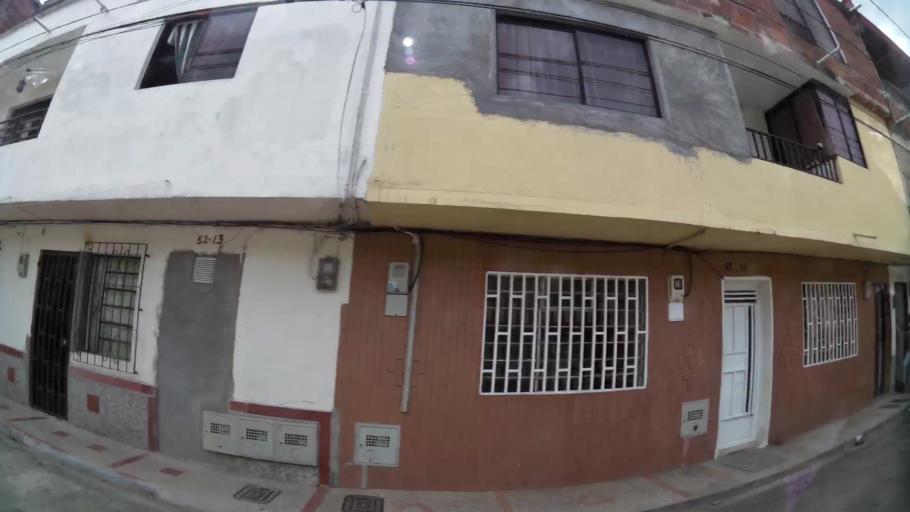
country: CO
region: Antioquia
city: Municipio de Copacabana
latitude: 6.3498
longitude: -75.5051
